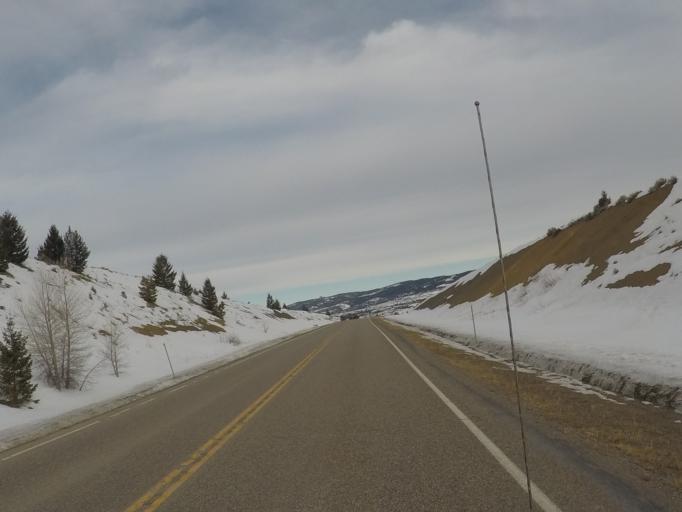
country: US
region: Montana
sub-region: Meagher County
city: White Sulphur Springs
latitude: 46.6453
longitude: -110.8664
